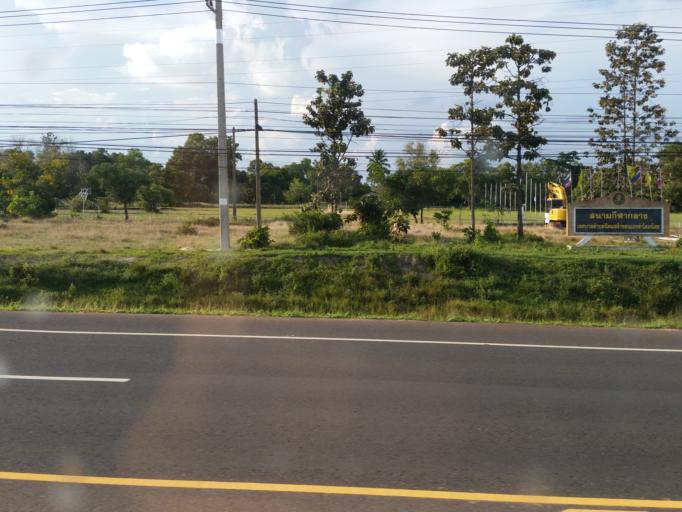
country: TH
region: Changwat Ubon Ratchathani
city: Sirindhorn
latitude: 15.2008
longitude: 105.3860
